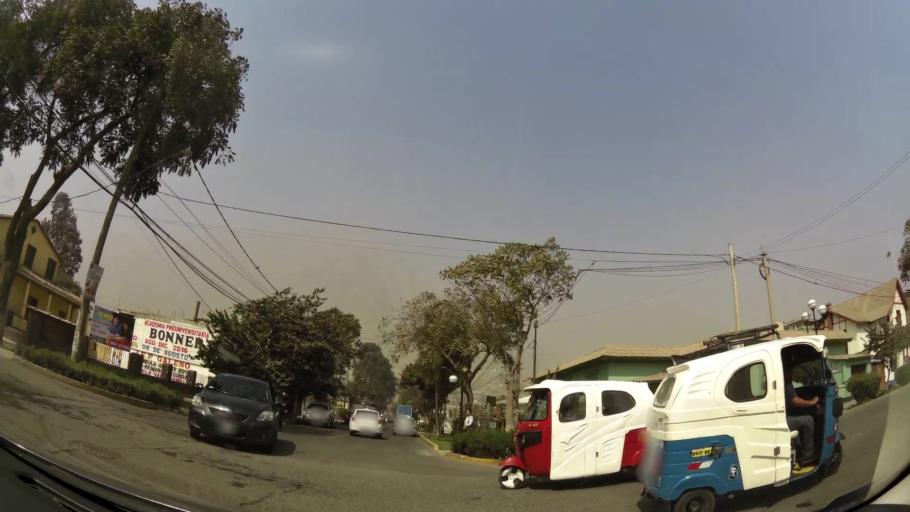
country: PE
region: Lima
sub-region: Lima
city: Asentamiento Humano Nicolas de Pierola
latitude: -11.9378
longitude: -76.6986
